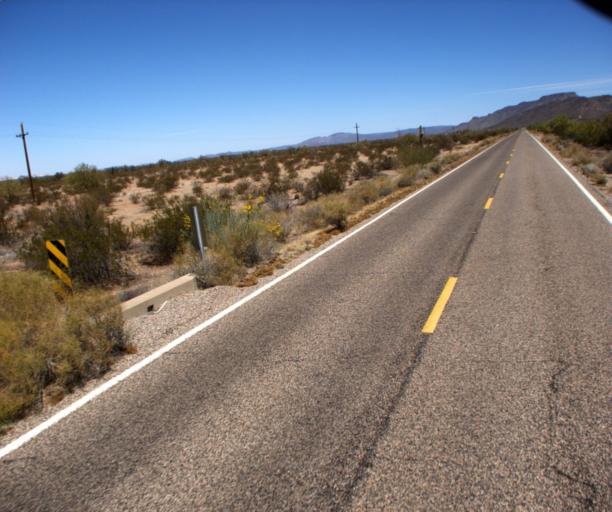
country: US
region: Arizona
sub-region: Pima County
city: Ajo
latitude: 32.2413
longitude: -112.7493
